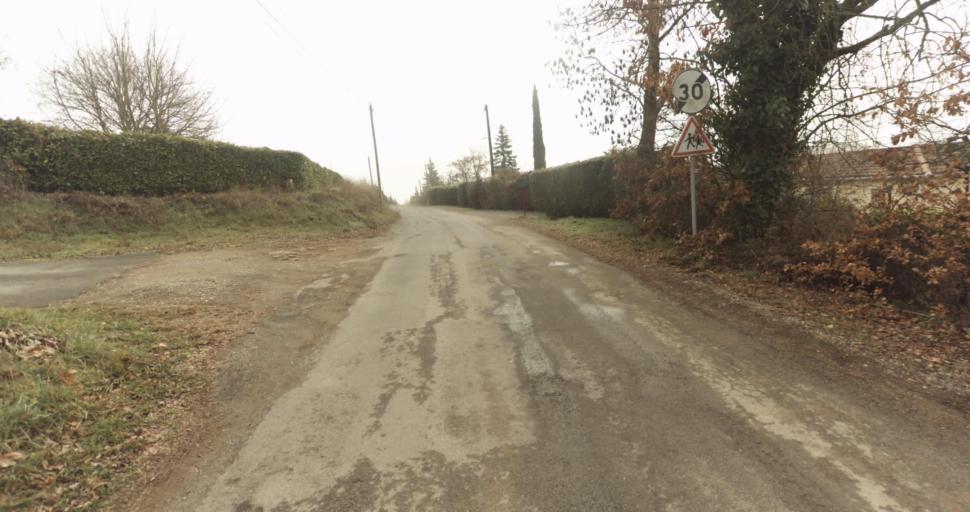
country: FR
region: Midi-Pyrenees
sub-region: Departement du Lot
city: Figeac
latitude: 44.6296
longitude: 2.0199
